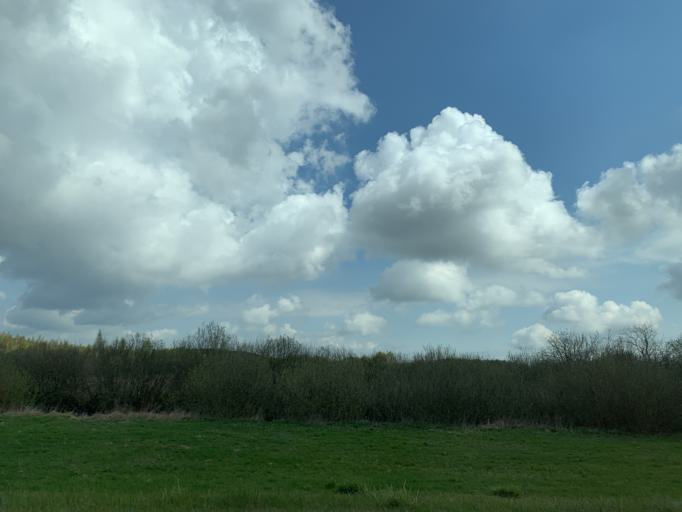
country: BY
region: Minsk
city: Nyasvizh
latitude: 53.2427
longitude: 26.7063
